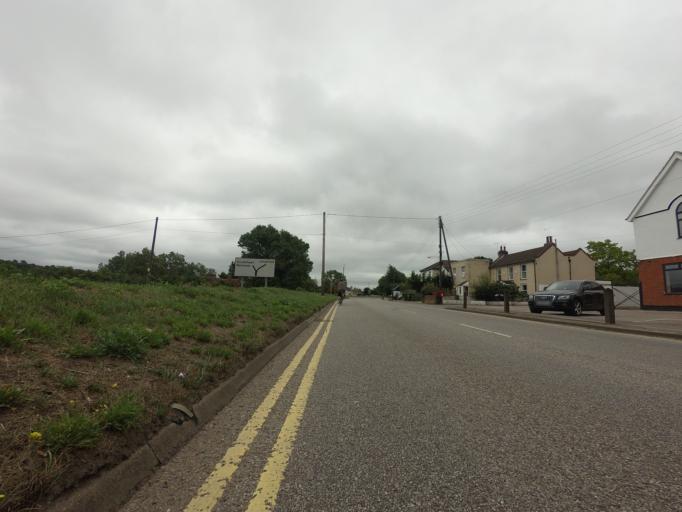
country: GB
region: England
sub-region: Kent
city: Longfield
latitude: 51.4139
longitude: 0.2770
